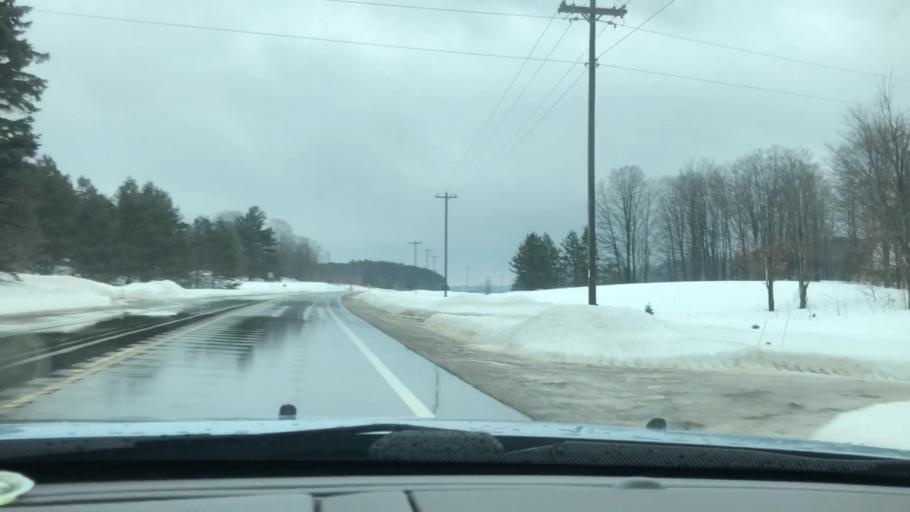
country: US
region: Michigan
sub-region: Charlevoix County
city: Boyne City
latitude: 45.0965
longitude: -84.9859
